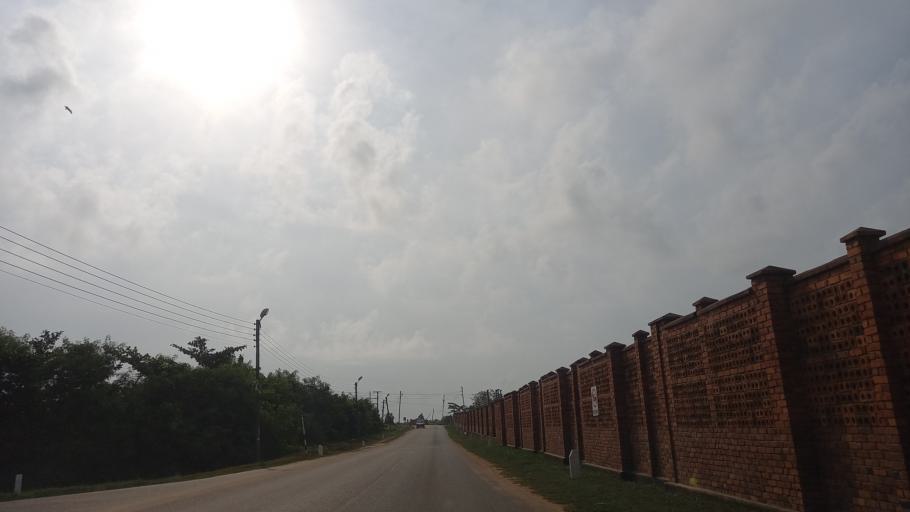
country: GH
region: Western
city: Shama Junction
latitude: 4.9753
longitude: -1.6571
